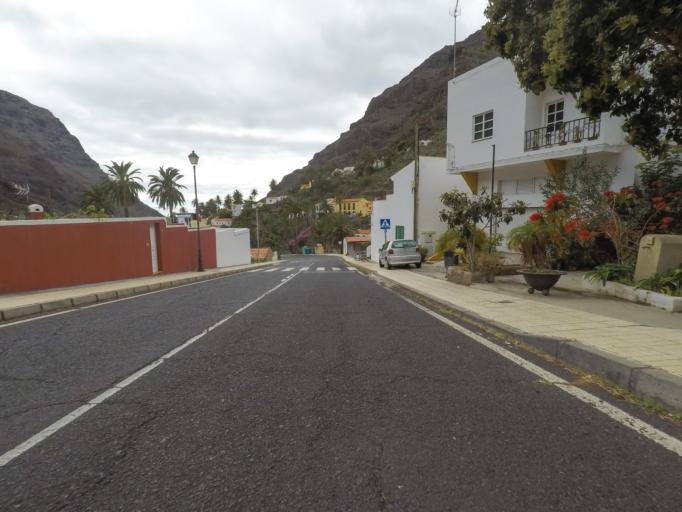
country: ES
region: Canary Islands
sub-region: Provincia de Santa Cruz de Tenerife
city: Vallehermosa
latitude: 28.1082
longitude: -17.3254
